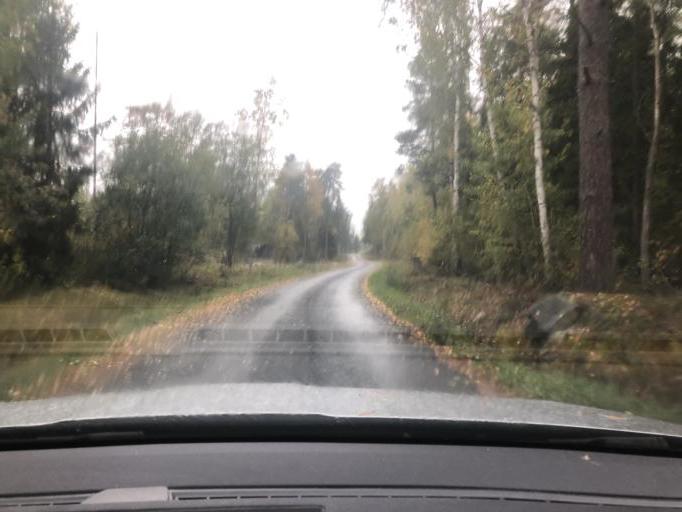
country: SE
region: Vaestmanland
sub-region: Kungsors Kommun
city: Kungsoer
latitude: 59.2273
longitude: 16.0851
